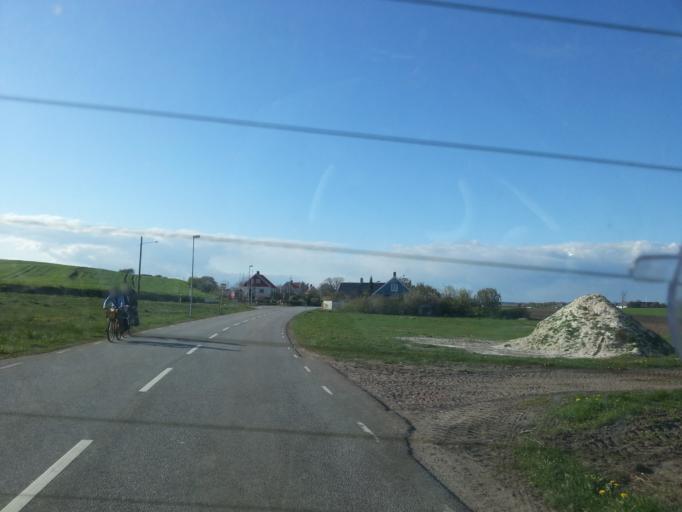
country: SE
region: Skane
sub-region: Ystads Kommun
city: Kopingebro
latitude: 55.4062
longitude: 14.0204
